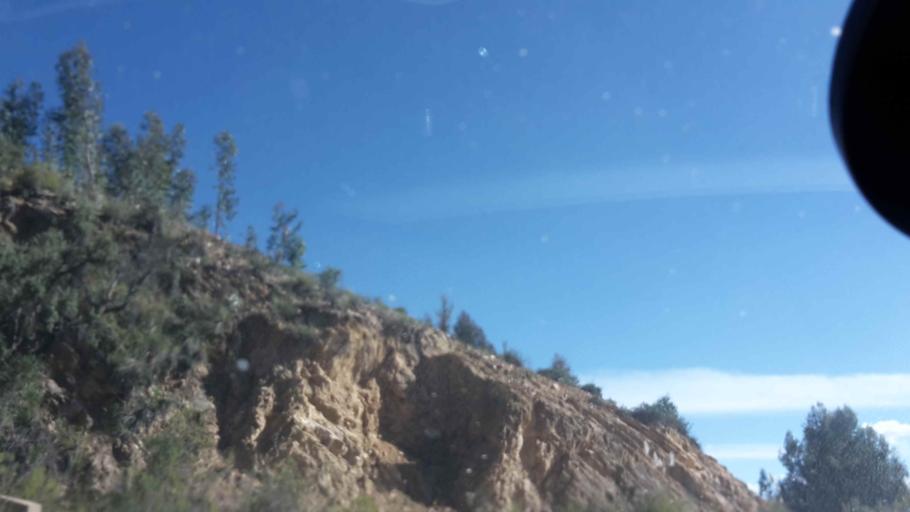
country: BO
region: Cochabamba
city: Arani
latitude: -17.6775
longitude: -65.7234
